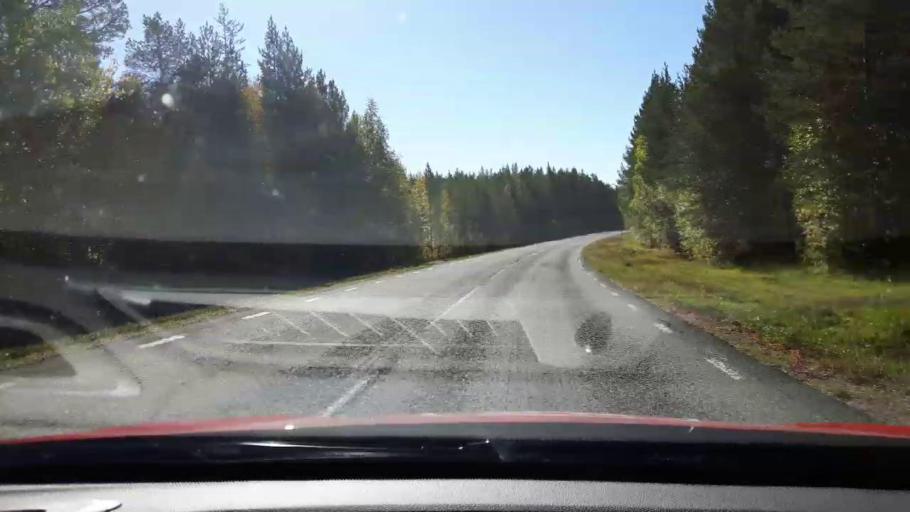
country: SE
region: Jaemtland
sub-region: Harjedalens Kommun
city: Sveg
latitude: 62.3252
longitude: 14.0617
